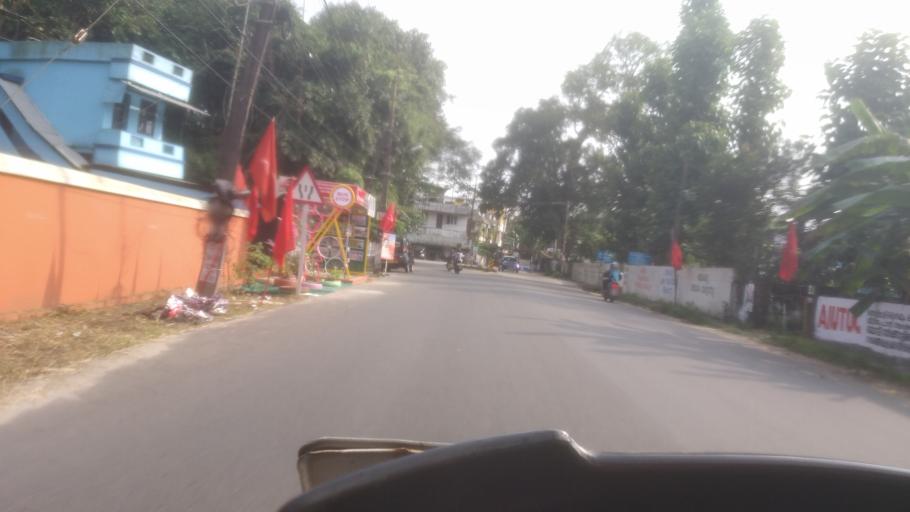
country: IN
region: Kerala
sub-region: Alappuzha
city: Arukutti
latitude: 9.9243
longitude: 76.3565
